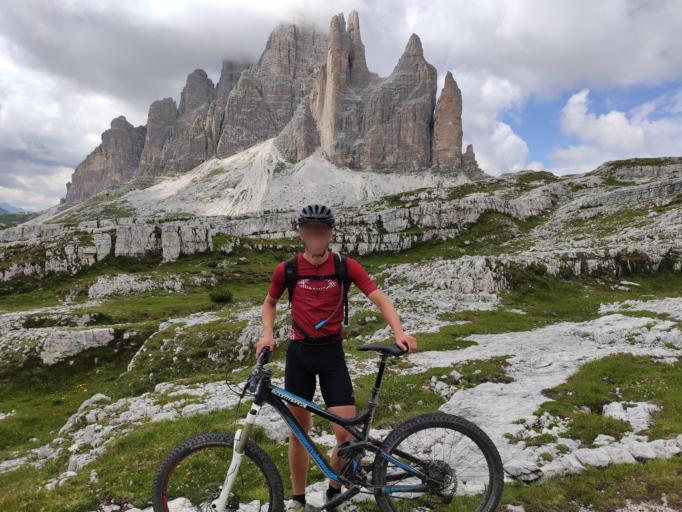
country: IT
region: Trentino-Alto Adige
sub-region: Bolzano
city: Sesto
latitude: 46.6147
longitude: 12.3200
